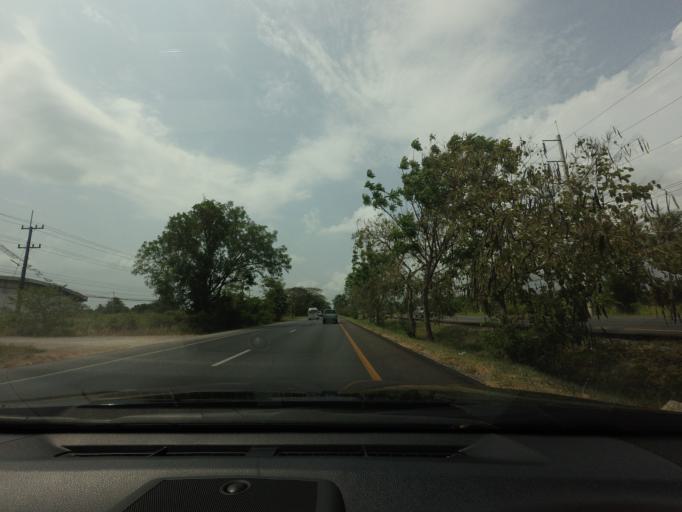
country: TH
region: Prachuap Khiri Khan
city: Prachuap Khiri Khan
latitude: 11.8854
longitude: 99.7891
